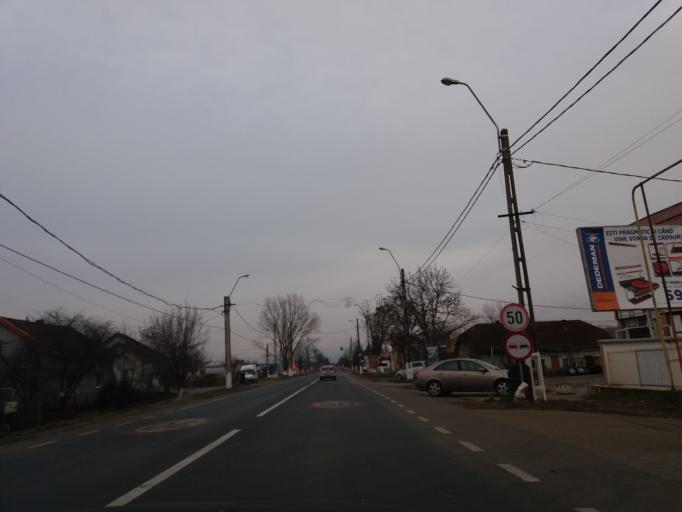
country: RO
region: Hunedoara
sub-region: Comuna Calan
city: Calan
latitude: 45.7341
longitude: 22.9972
